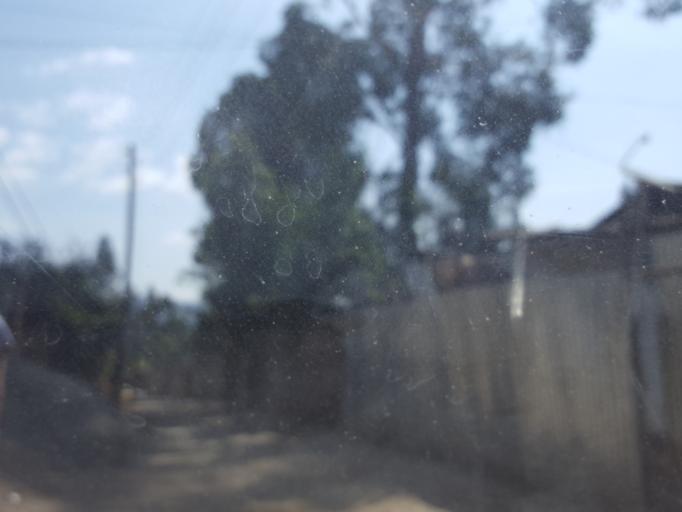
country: ET
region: Adis Abeba
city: Addis Ababa
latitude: 9.0632
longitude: 38.7630
